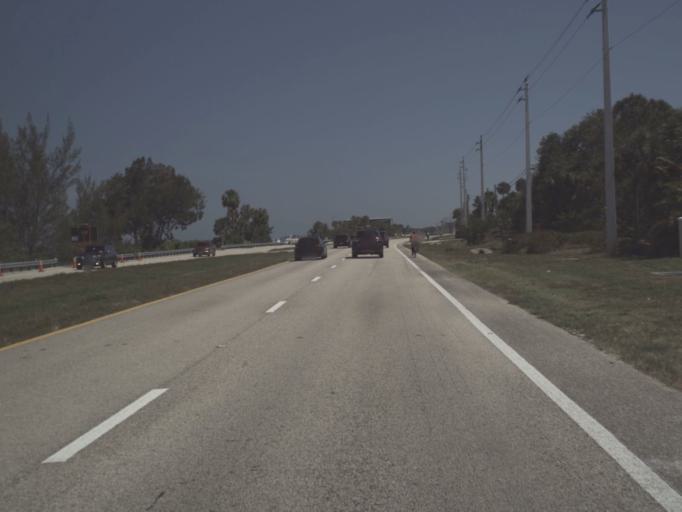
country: US
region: Florida
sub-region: Brevard County
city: Micco
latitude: 27.8779
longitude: -80.5000
